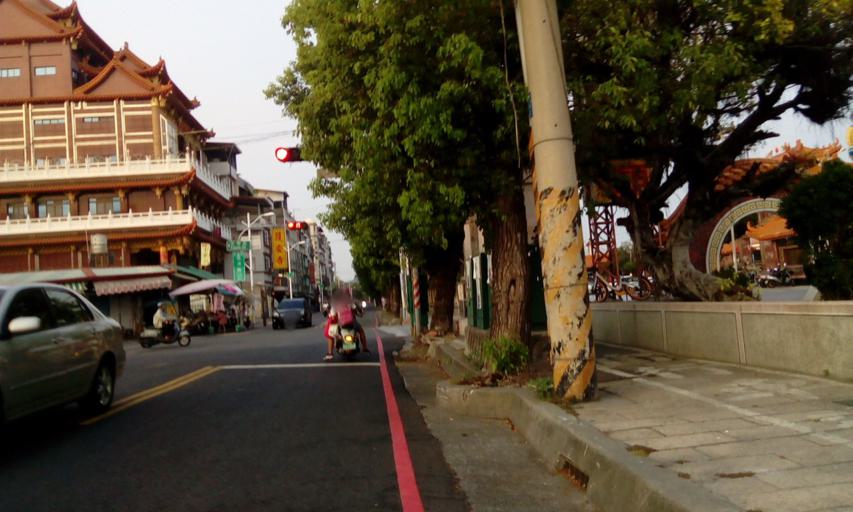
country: TW
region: Kaohsiung
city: Kaohsiung
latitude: 22.6848
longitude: 120.2948
